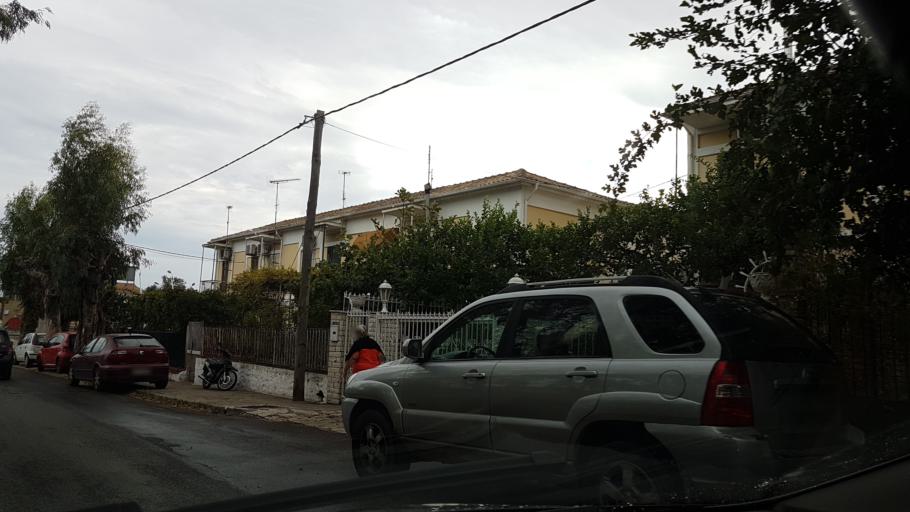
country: GR
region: Ionian Islands
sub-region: Nomos Kerkyras
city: Alepou
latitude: 39.6169
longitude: 19.9077
